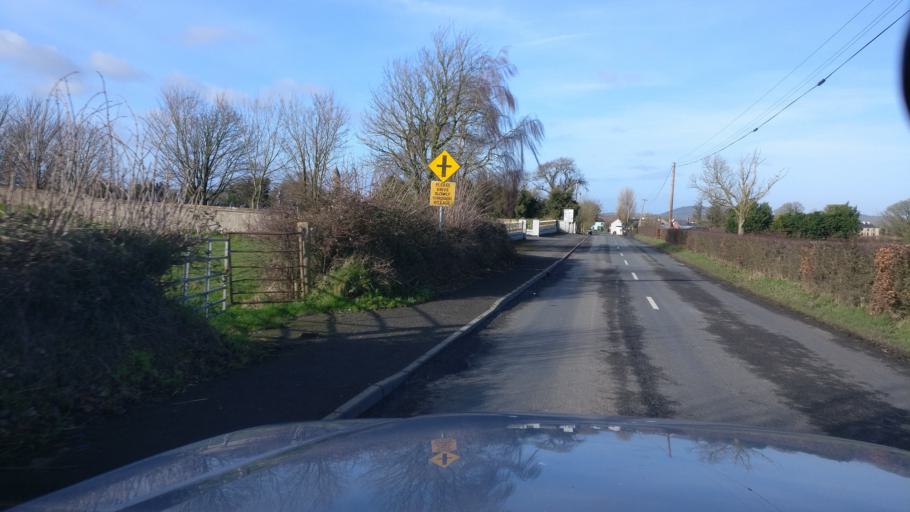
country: IE
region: Leinster
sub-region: Laois
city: Stradbally
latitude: 52.9577
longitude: -7.1999
